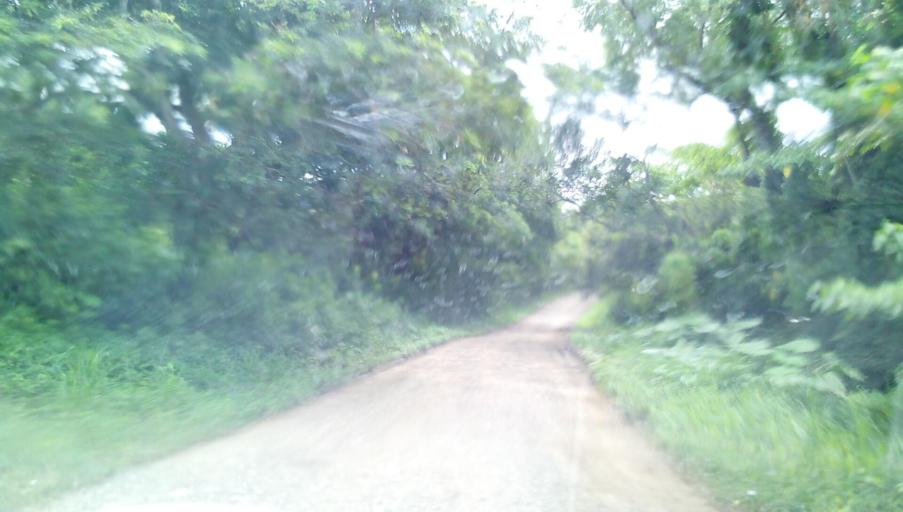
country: MX
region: Veracruz
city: Tepetzintla
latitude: 21.1381
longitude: -97.8510
